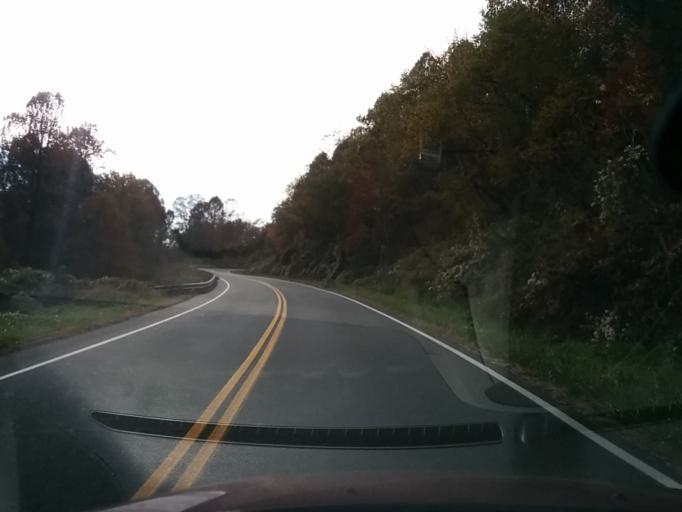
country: US
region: Virginia
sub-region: Nelson County
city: Nellysford
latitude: 37.9028
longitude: -78.9792
